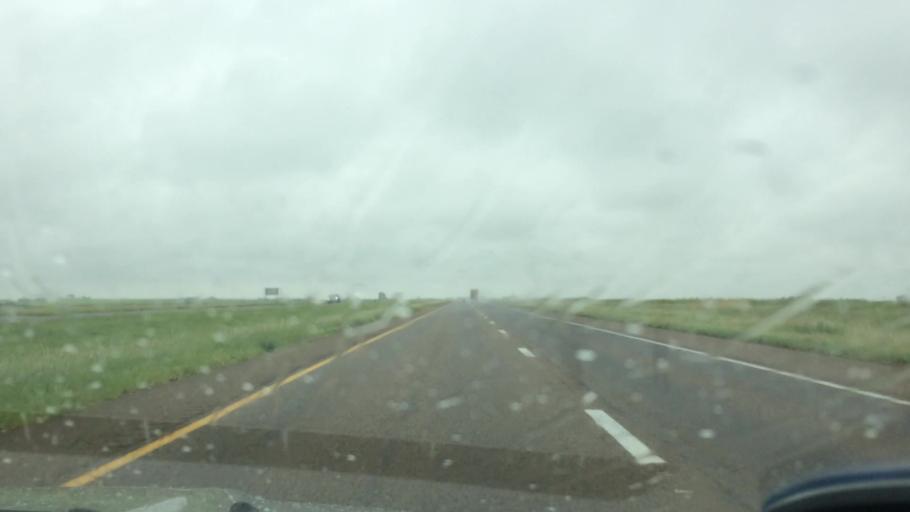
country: US
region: Kansas
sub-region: Ellis County
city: Victoria
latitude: 38.8638
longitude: -99.0325
